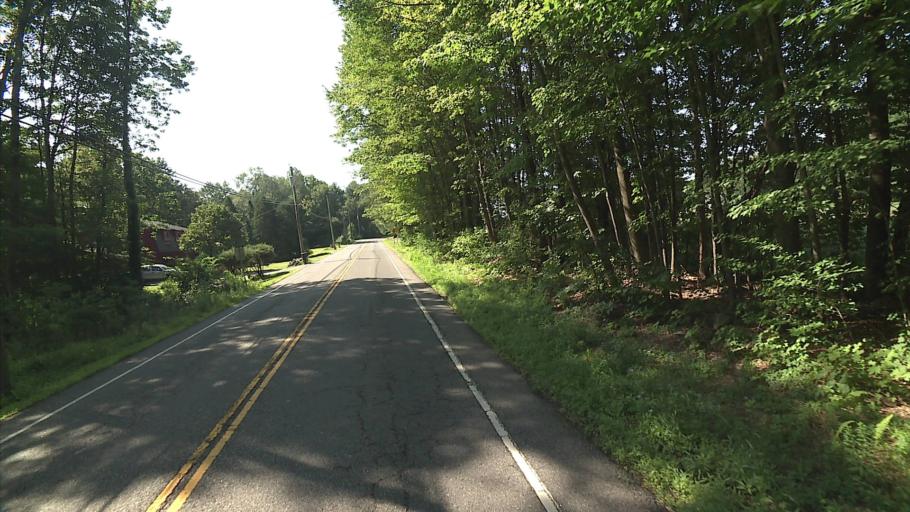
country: US
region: Connecticut
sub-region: Litchfield County
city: Winsted
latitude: 41.8870
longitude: -73.0654
